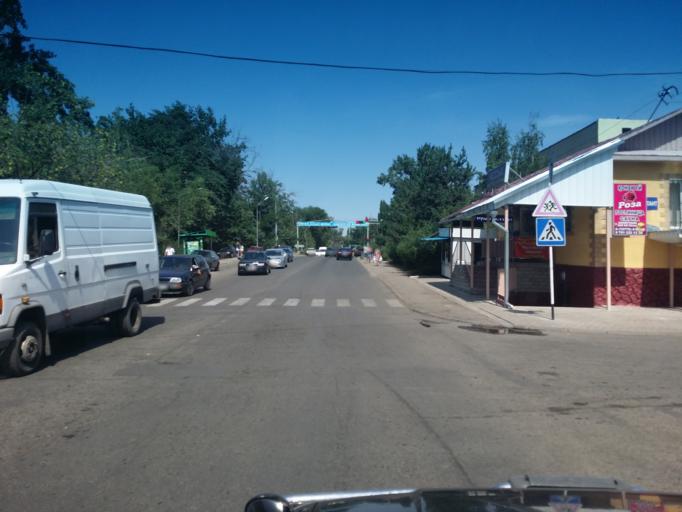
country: KZ
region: Almaty Oblysy
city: Esik
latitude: 43.3533
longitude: 77.4640
